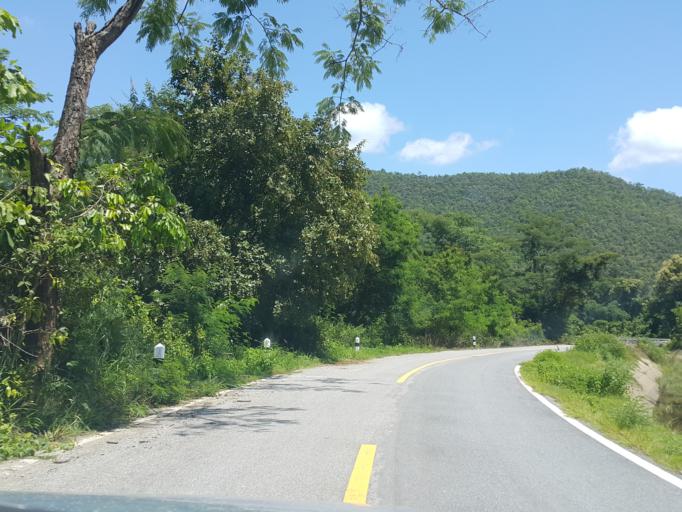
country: TH
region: Lamphun
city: Ban Thi
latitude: 18.6849
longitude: 99.1771
